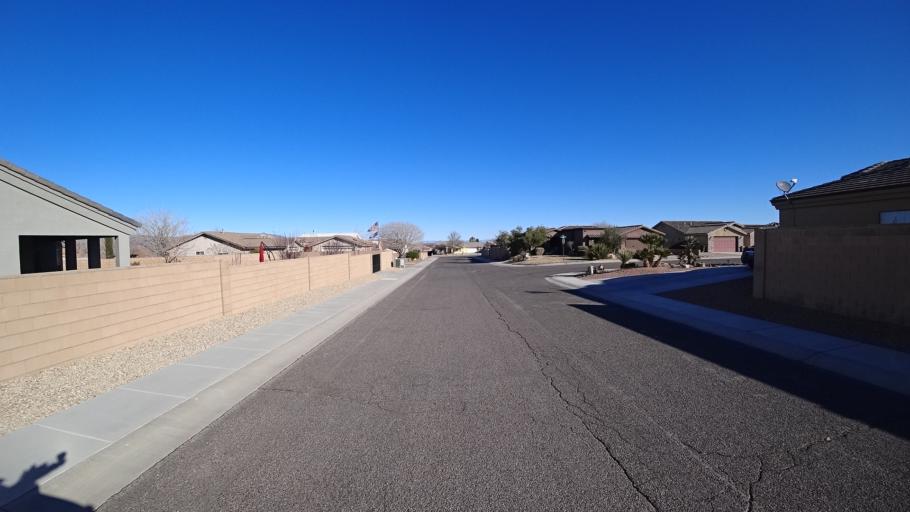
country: US
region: Arizona
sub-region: Mohave County
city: Kingman
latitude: 35.1846
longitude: -113.9998
